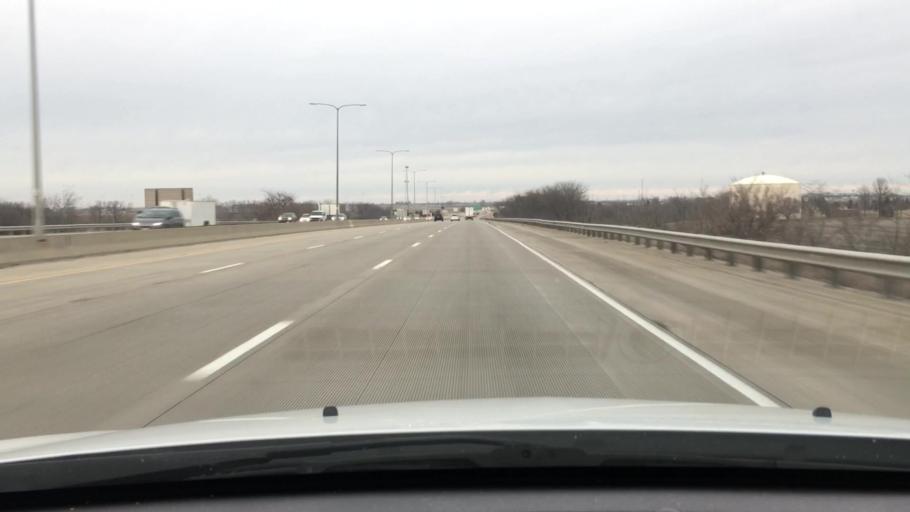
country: US
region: Illinois
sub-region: McLean County
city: Normal
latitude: 40.5063
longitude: -89.0287
